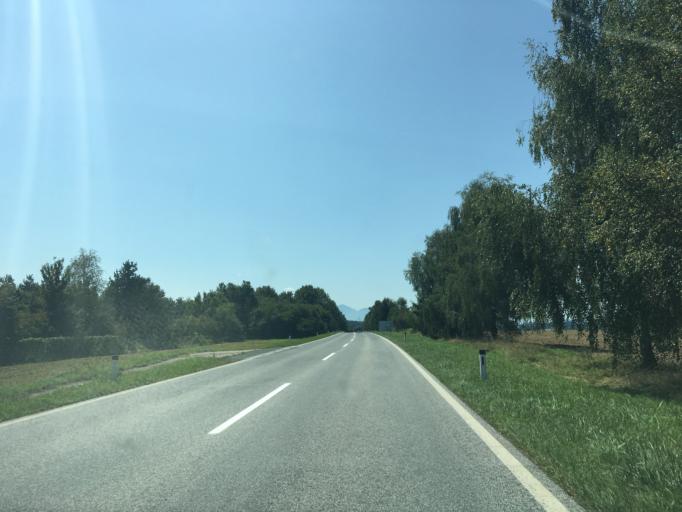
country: AT
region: Carinthia
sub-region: Politischer Bezirk Volkermarkt
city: Griffen
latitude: 46.6965
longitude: 14.7157
